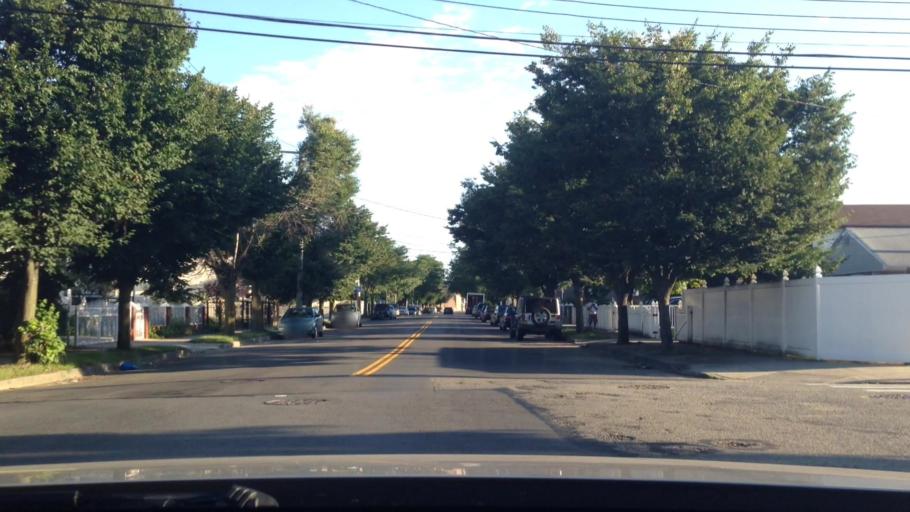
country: US
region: New York
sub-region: Nassau County
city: South Valley Stream
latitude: 40.6622
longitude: -73.7289
